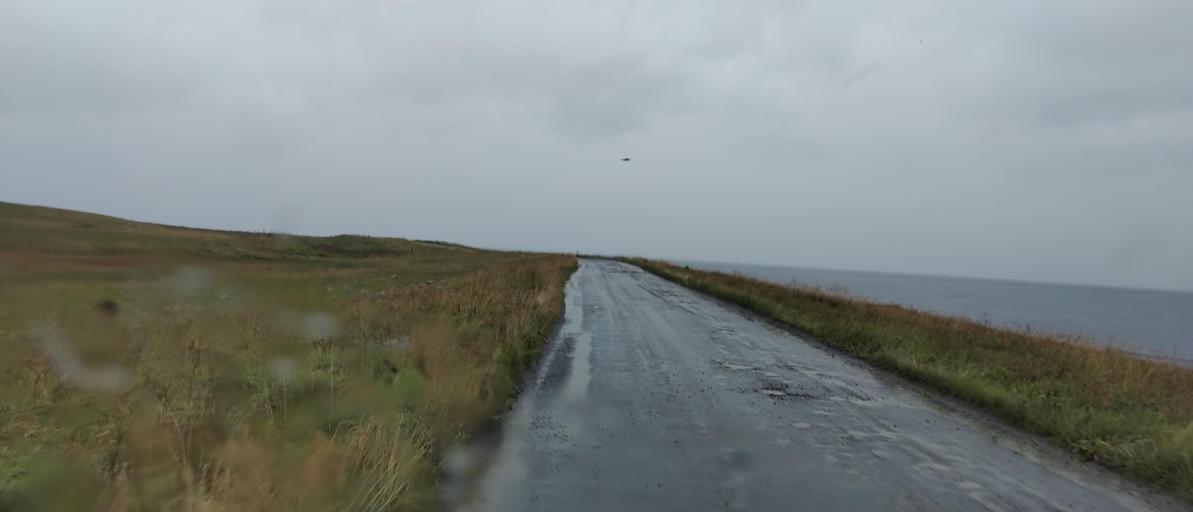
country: NO
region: Nordland
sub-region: Vestvagoy
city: Evjen
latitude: 68.3097
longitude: 13.6619
